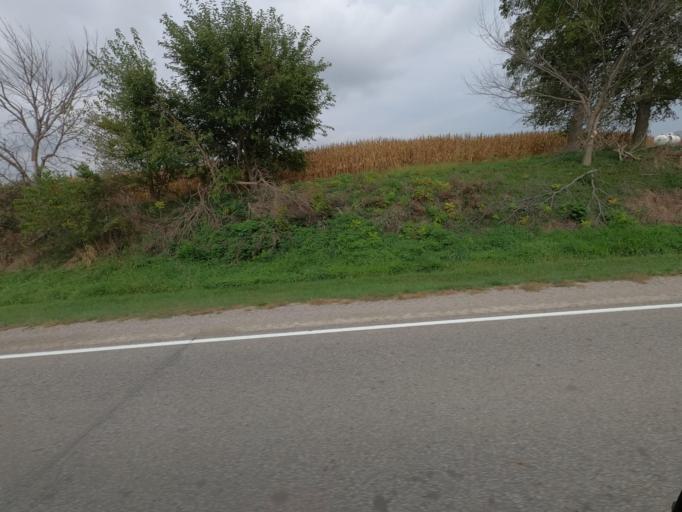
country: US
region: Iowa
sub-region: Wapello County
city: Ottumwa
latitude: 40.9052
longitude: -92.2021
